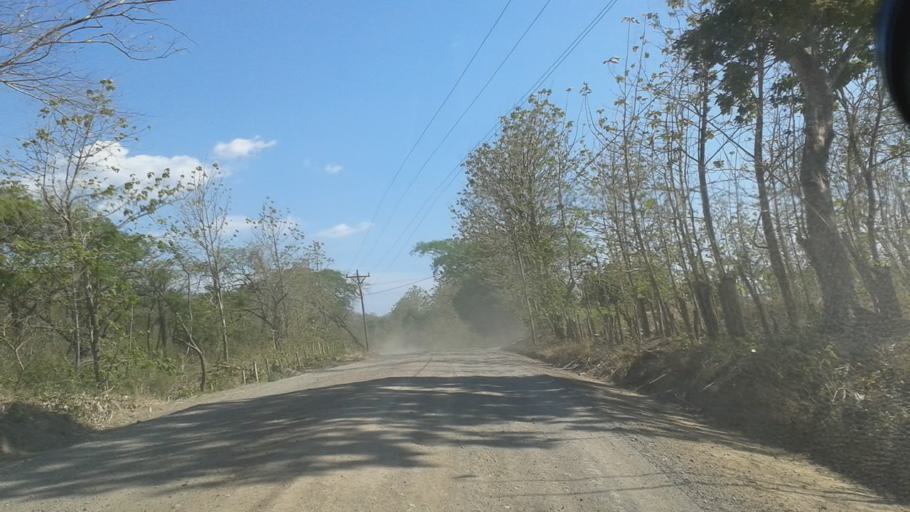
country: CR
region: Guanacaste
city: Santa Cruz
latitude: 10.1806
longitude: -85.7793
